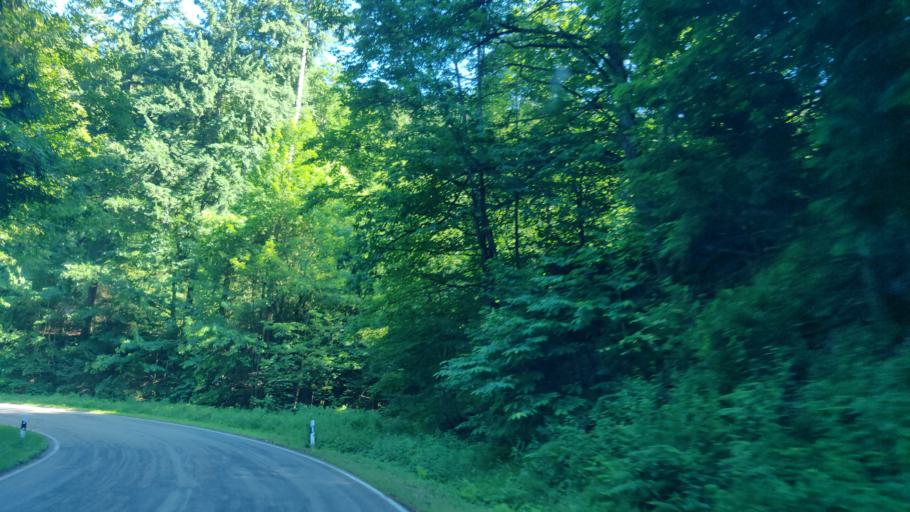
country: DE
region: Baden-Wuerttemberg
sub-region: Karlsruhe Region
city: Gernsbach
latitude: 48.7506
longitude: 8.3185
